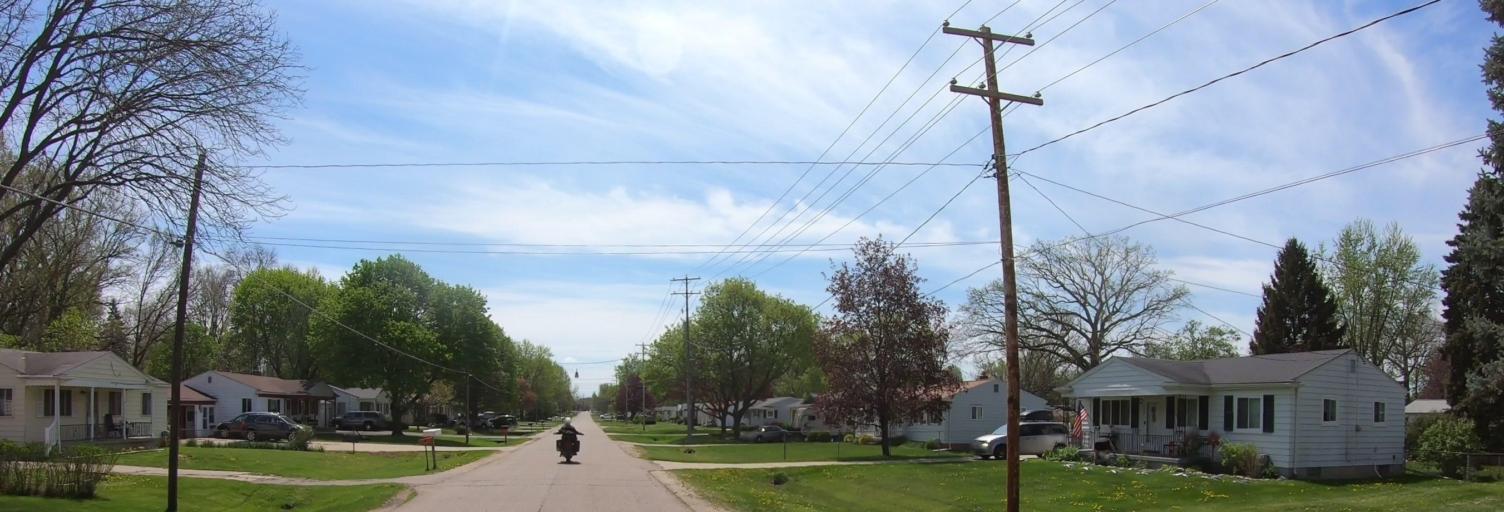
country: US
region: Michigan
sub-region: Genesee County
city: Flint
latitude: 42.9649
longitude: -83.7033
